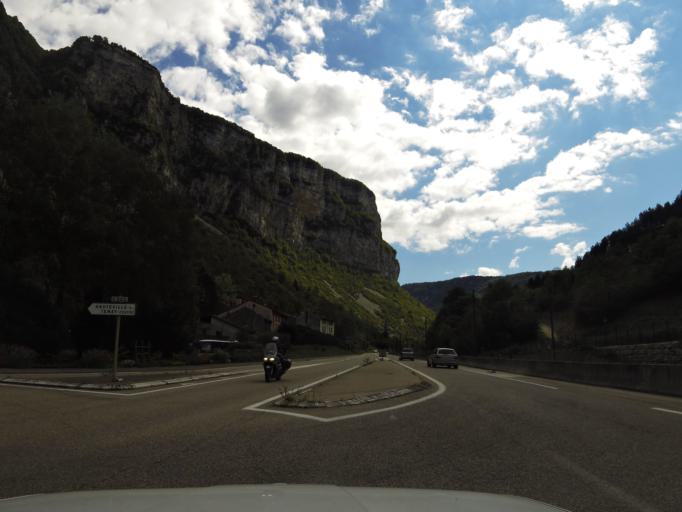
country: FR
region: Rhone-Alpes
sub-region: Departement de l'Ain
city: Tenay
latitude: 45.9124
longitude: 5.5097
